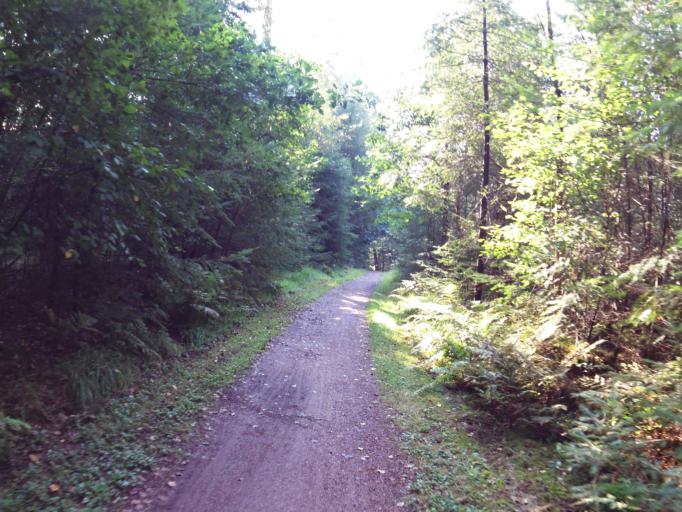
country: NL
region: Overijssel
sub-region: Gemeente Twenterand
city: Den Ham
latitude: 52.4965
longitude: 6.4576
